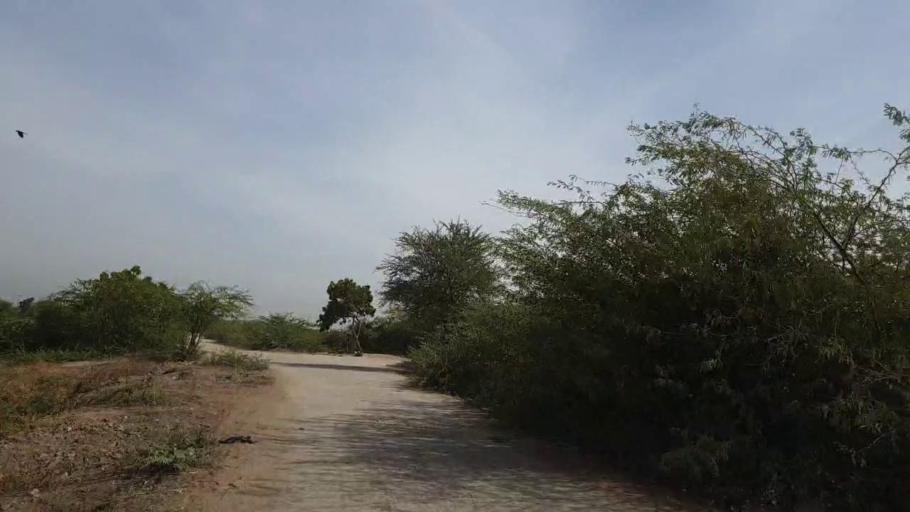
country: PK
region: Sindh
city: Kunri
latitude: 25.1794
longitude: 69.6325
